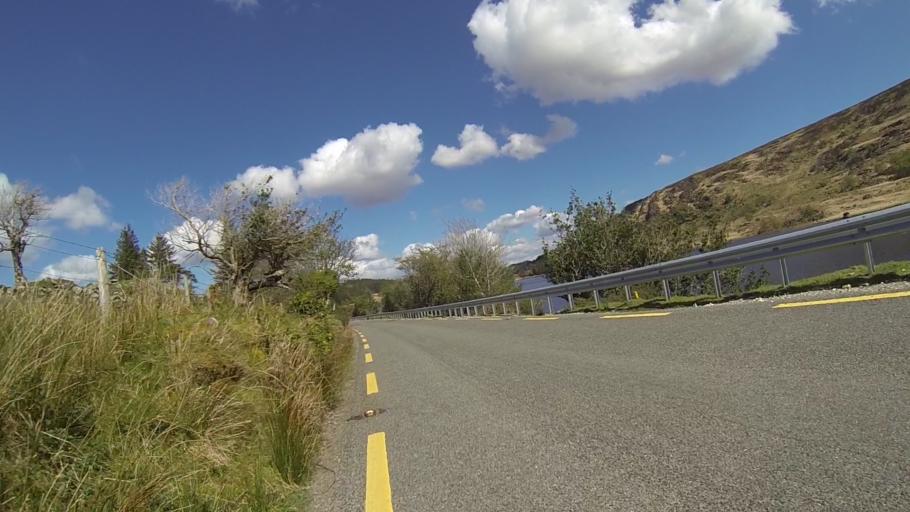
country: IE
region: Munster
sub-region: Ciarrai
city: Kenmare
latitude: 51.9555
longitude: -9.6232
